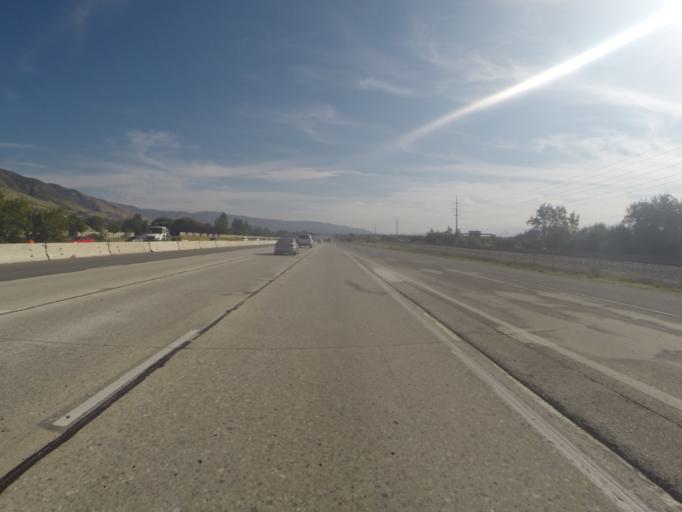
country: US
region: Utah
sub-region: Davis County
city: Farmington
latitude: 40.9631
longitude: -111.8914
